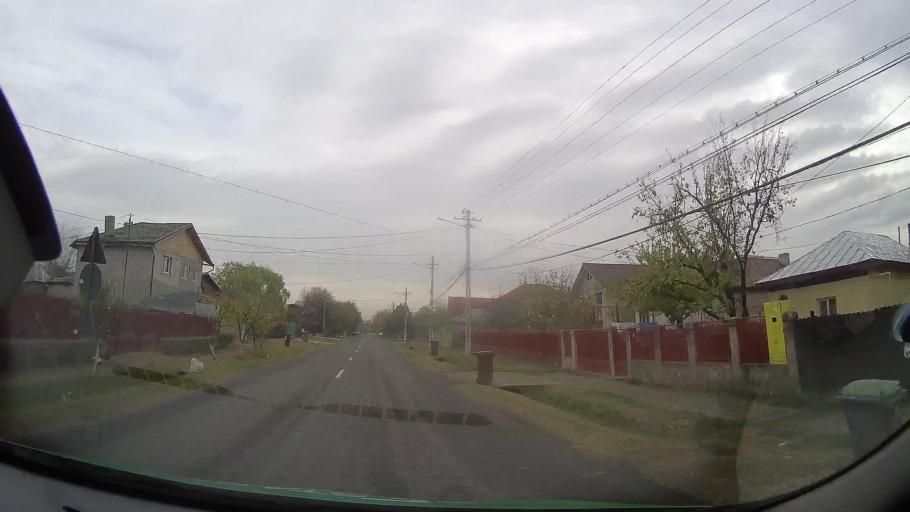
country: RO
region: Prahova
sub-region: Comuna Berceni
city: Berceni
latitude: 44.9351
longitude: 26.1208
